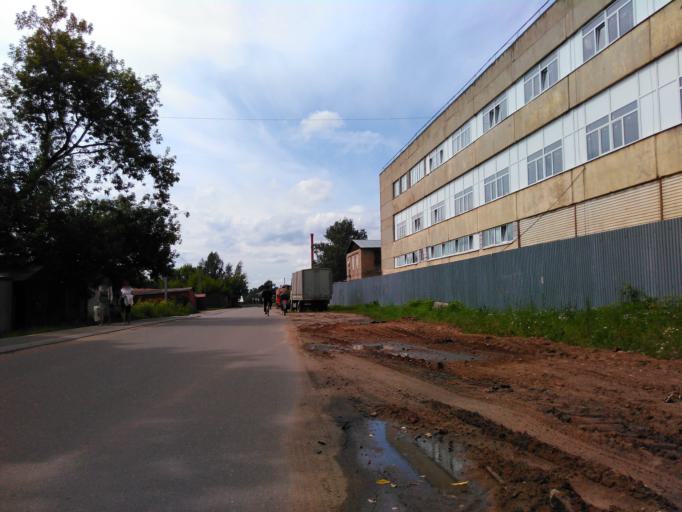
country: RU
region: Moskovskaya
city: Pravdinskiy
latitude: 56.0580
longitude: 37.8547
